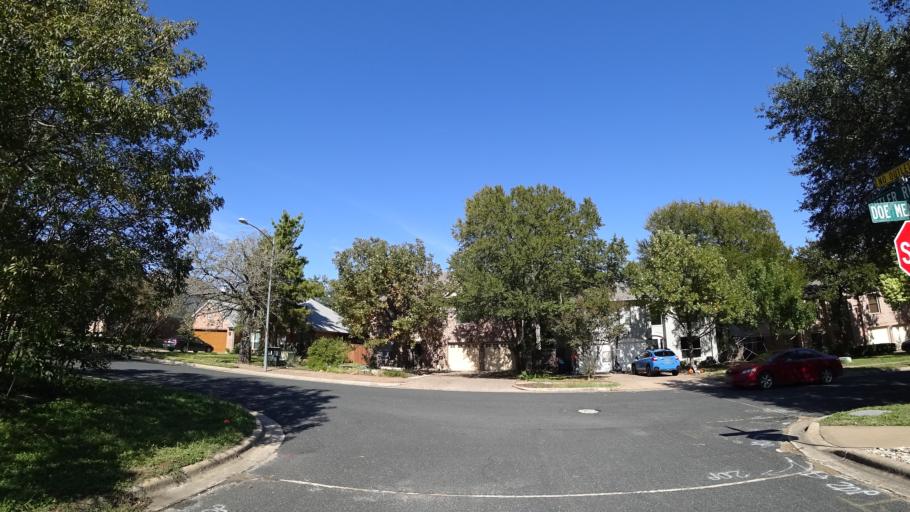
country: US
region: Texas
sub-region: Travis County
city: Shady Hollow
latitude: 30.2175
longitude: -97.8687
